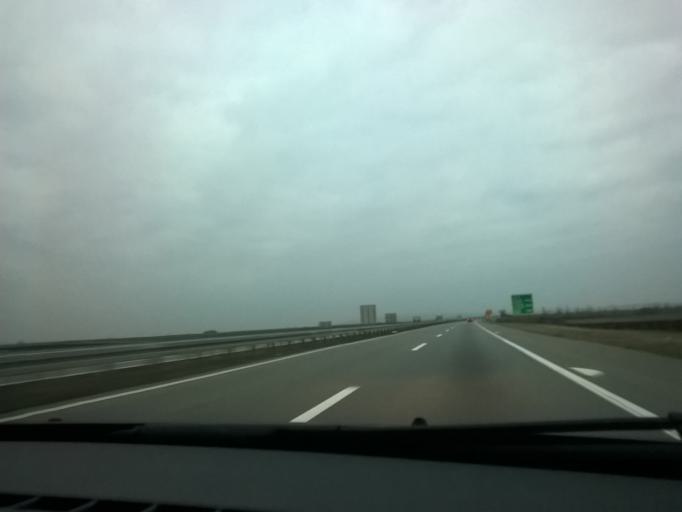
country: RS
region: Autonomna Pokrajina Vojvodina
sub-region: Juznobacki Okrug
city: Kovilj
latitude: 45.2394
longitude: 20.0395
